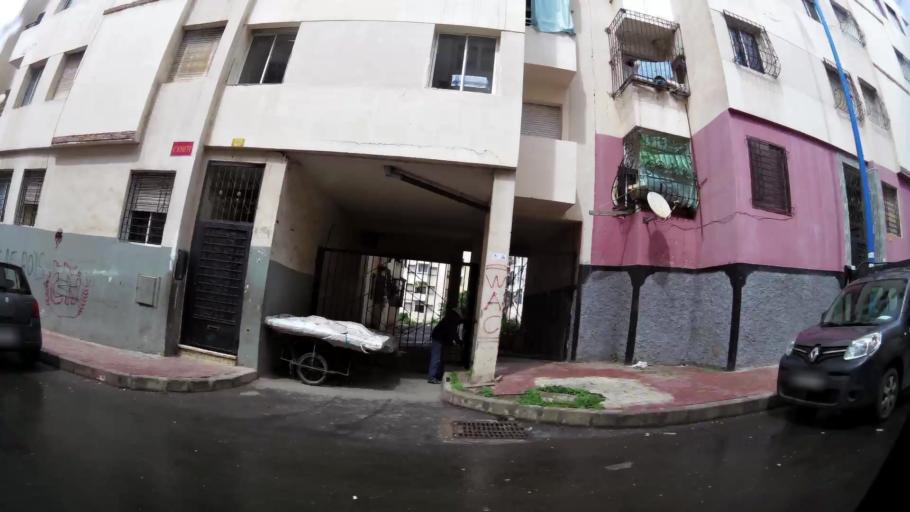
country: MA
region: Grand Casablanca
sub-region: Casablanca
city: Casablanca
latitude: 33.5294
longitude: -7.6468
